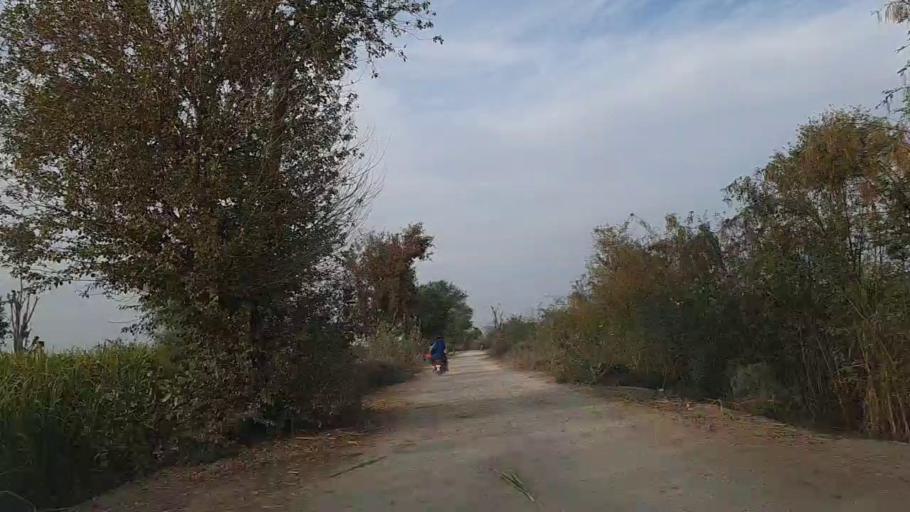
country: PK
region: Sindh
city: Daur
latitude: 26.5242
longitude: 68.4073
